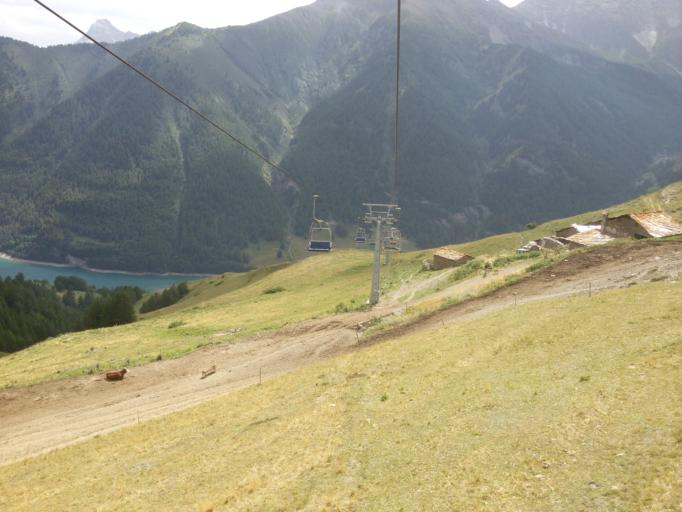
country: IT
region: Piedmont
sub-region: Provincia di Cuneo
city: Pontechianale
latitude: 44.6311
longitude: 7.0364
